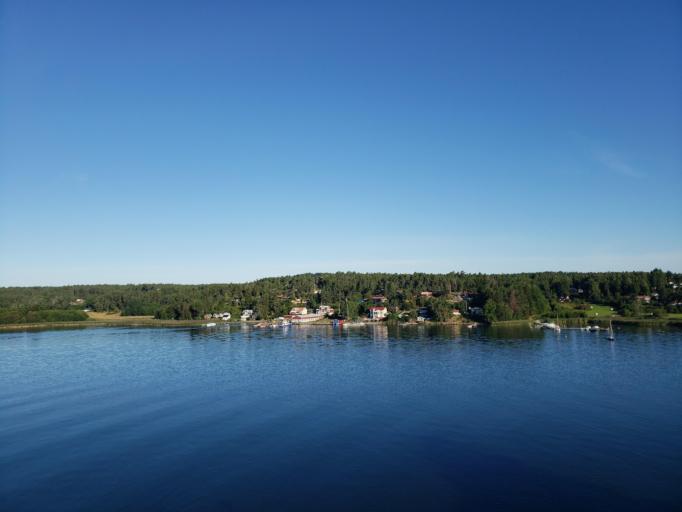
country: SE
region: Stockholm
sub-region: Vaxholms Kommun
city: Vaxholm
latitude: 59.5007
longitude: 18.4696
